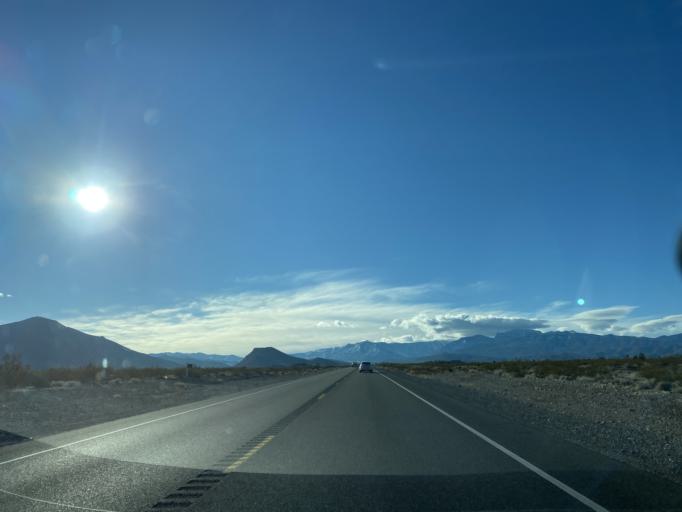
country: US
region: Nevada
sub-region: Clark County
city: Summerlin South
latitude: 36.3196
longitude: -115.3602
